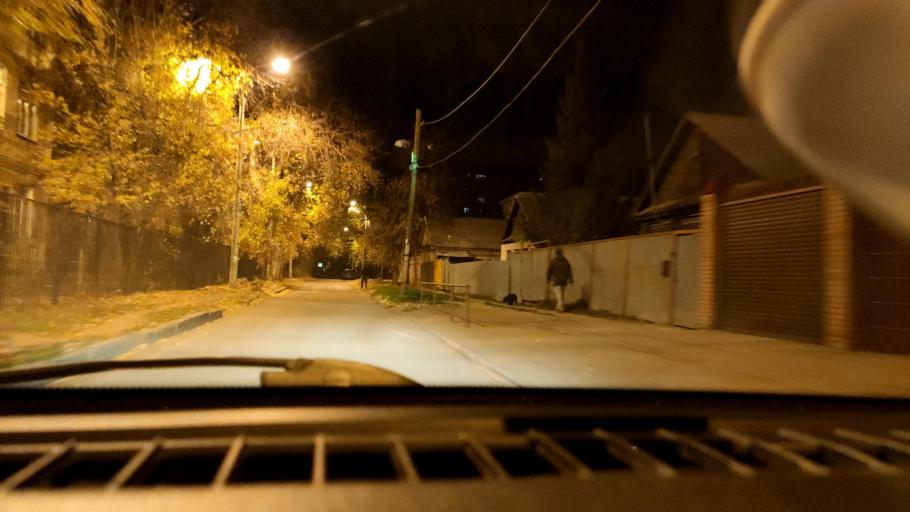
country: RU
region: Samara
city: Samara
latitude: 53.2020
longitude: 50.1860
